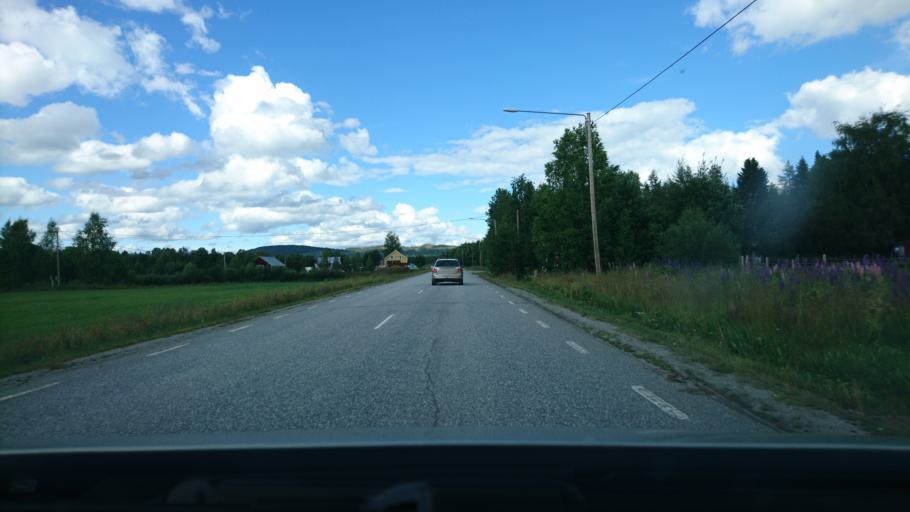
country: SE
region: Vaesterbotten
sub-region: Asele Kommun
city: Asele
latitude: 64.0149
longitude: 17.2937
